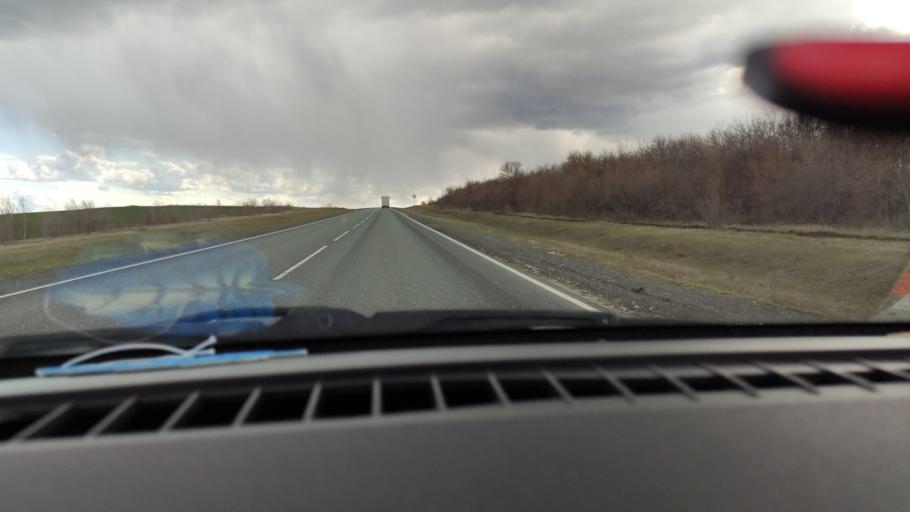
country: RU
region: Saratov
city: Balakovo
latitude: 52.1918
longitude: 47.8543
